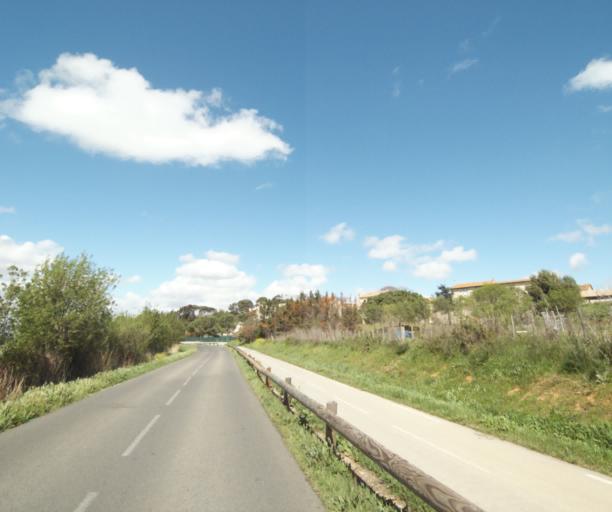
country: FR
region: Languedoc-Roussillon
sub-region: Departement de l'Herault
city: Lattes
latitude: 43.5616
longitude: 3.9223
